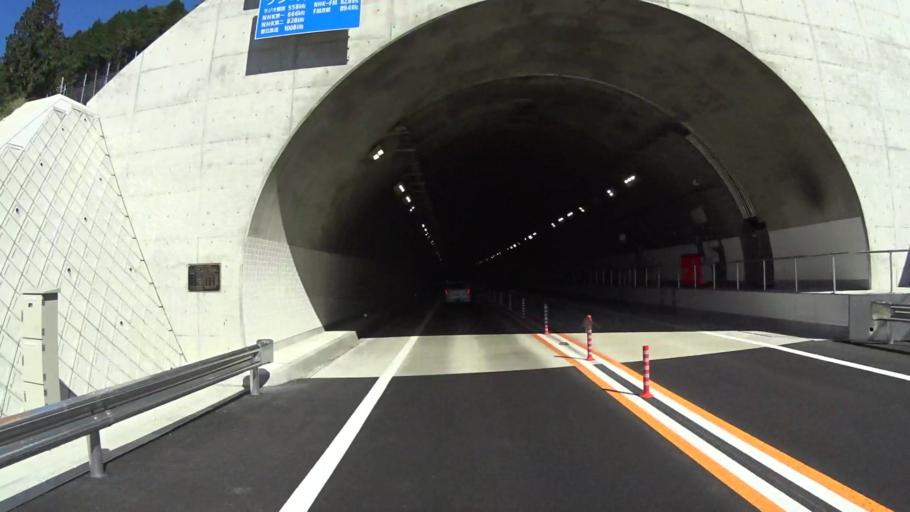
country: JP
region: Kyoto
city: Ayabe
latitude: 35.2278
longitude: 135.3449
